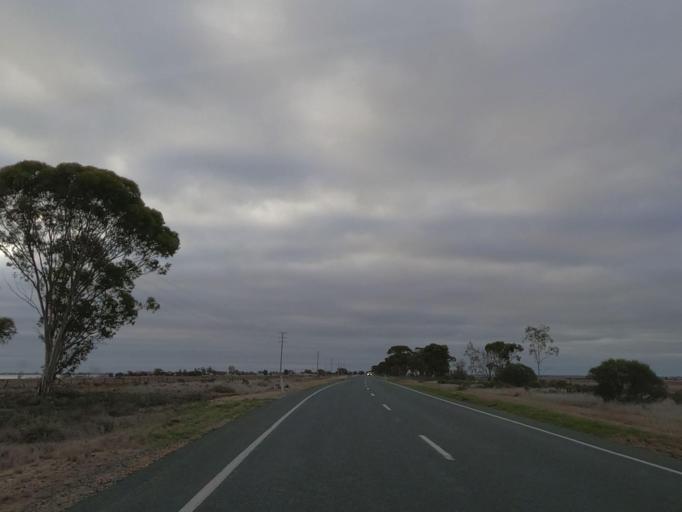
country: AU
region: Victoria
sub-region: Swan Hill
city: Swan Hill
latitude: -35.5917
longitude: 143.7905
